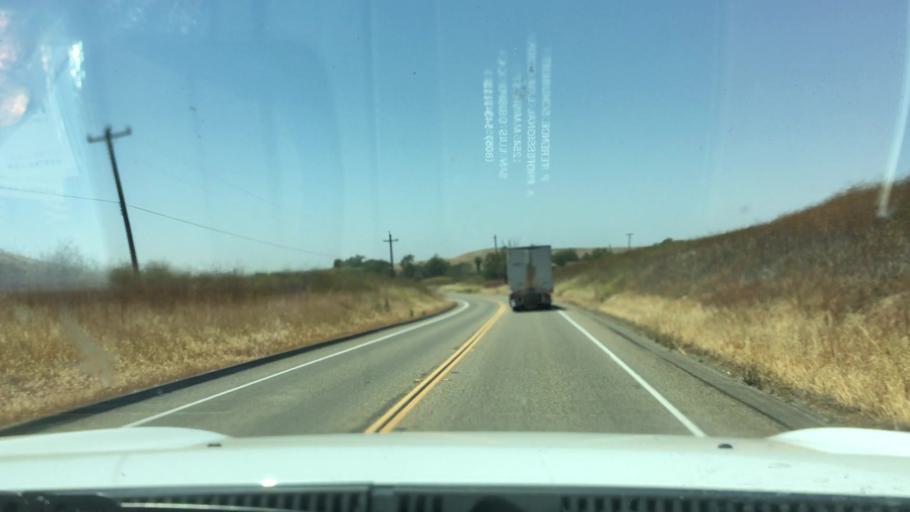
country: US
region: California
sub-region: Santa Barbara County
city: Santa Maria
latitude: 35.0001
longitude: -120.3902
